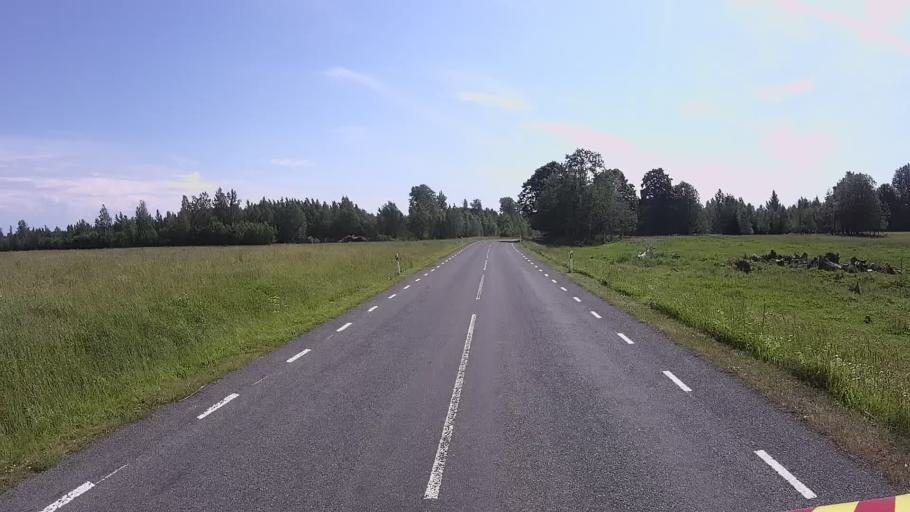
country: EE
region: Viljandimaa
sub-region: Karksi vald
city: Karksi-Nuia
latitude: 58.0477
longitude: 25.5456
